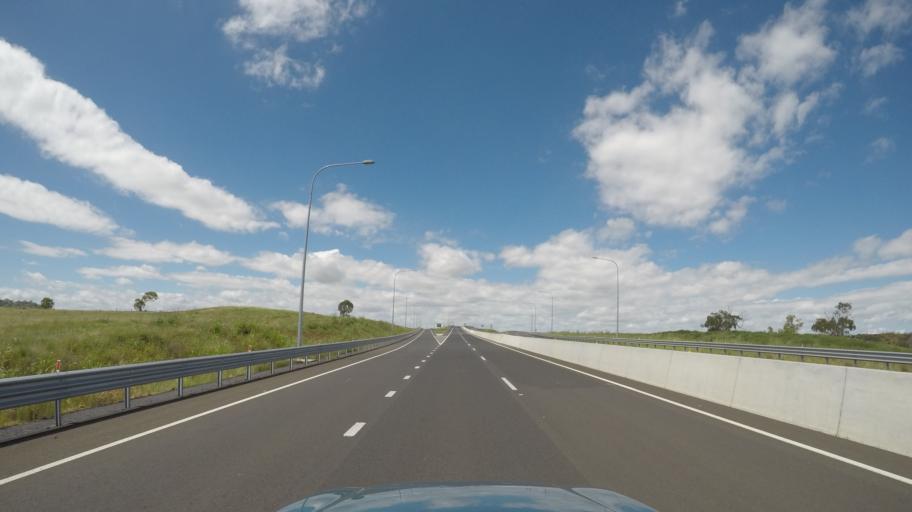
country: AU
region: Queensland
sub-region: Toowoomba
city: Wilsonton Heights
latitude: -27.5179
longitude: 151.8648
